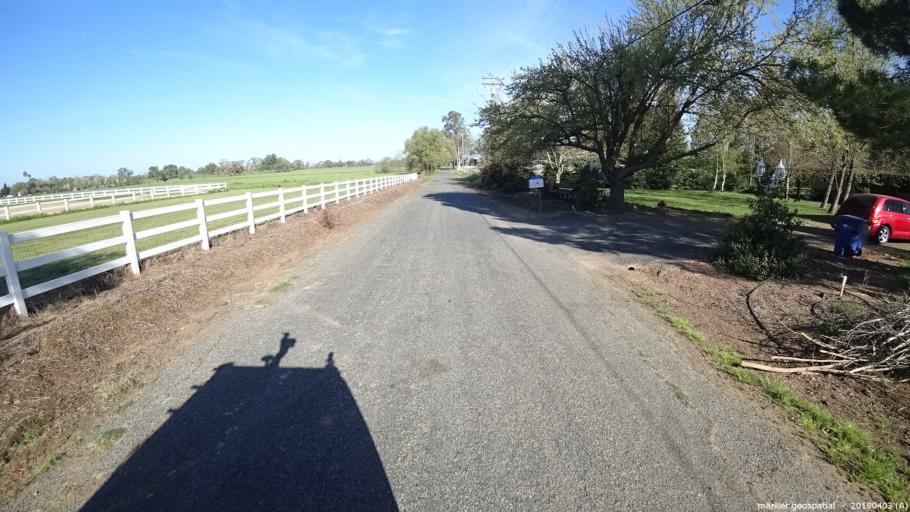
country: US
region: California
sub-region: Sacramento County
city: Wilton
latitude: 38.4332
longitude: -121.2054
